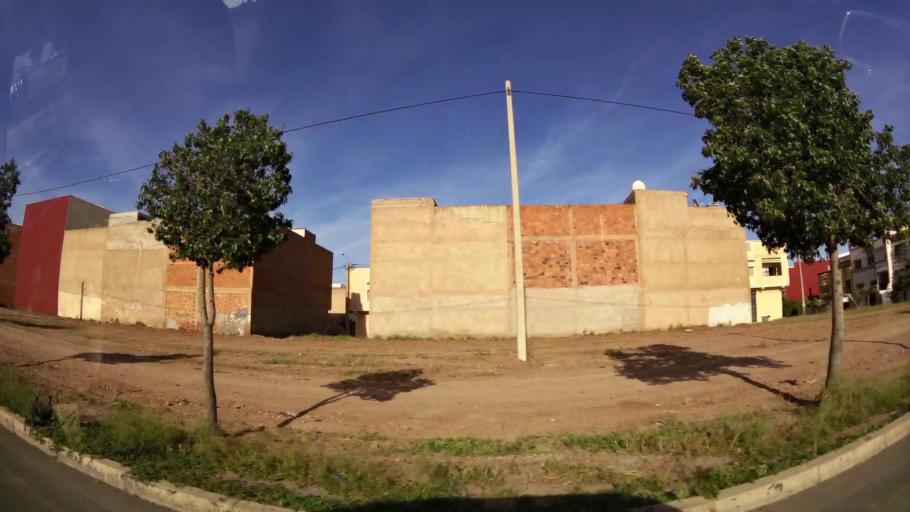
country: MA
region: Oriental
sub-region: Oujda-Angad
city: Oujda
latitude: 34.6696
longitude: -1.9000
